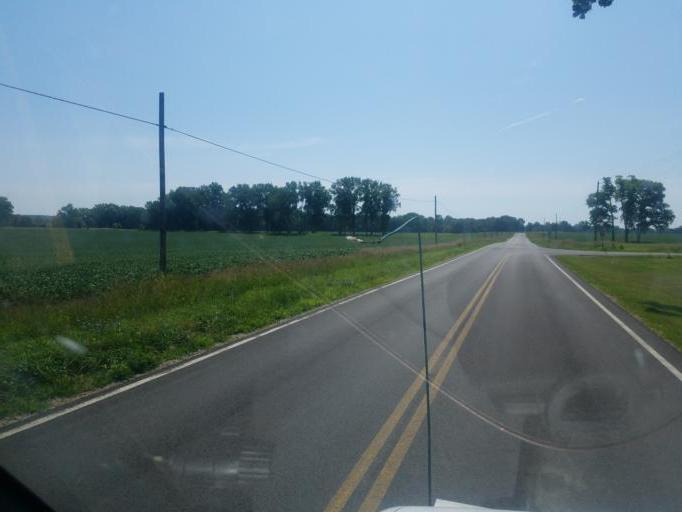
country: US
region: Ohio
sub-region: Champaign County
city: North Lewisburg
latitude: 40.2089
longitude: -83.4952
